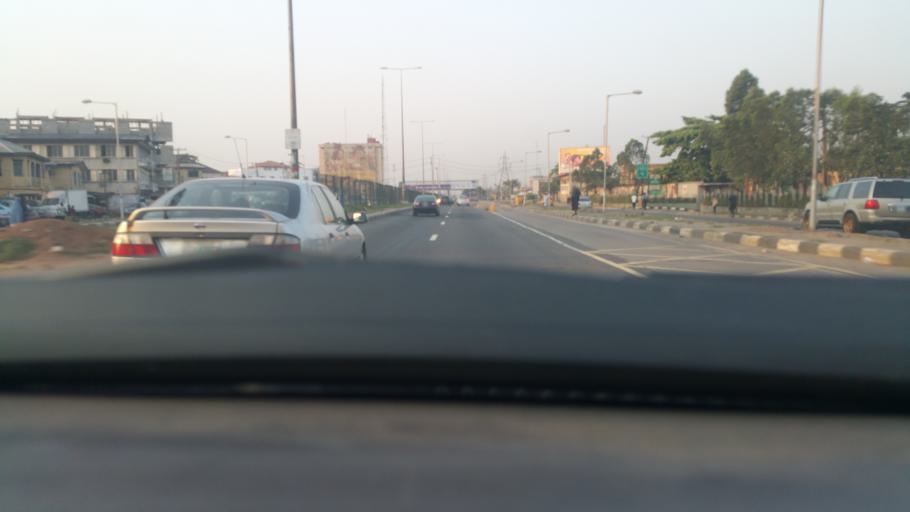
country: NG
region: Lagos
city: Somolu
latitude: 6.5294
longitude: 3.3675
